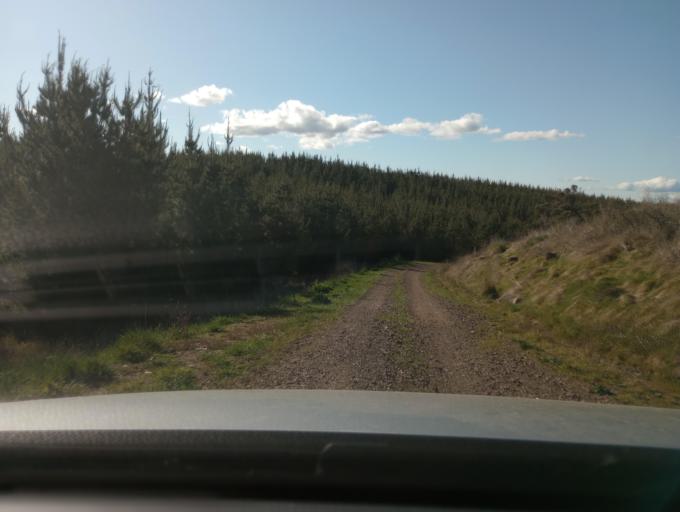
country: AU
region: New South Wales
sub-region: Blayney
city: Blayney
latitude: -33.4153
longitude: 149.3150
